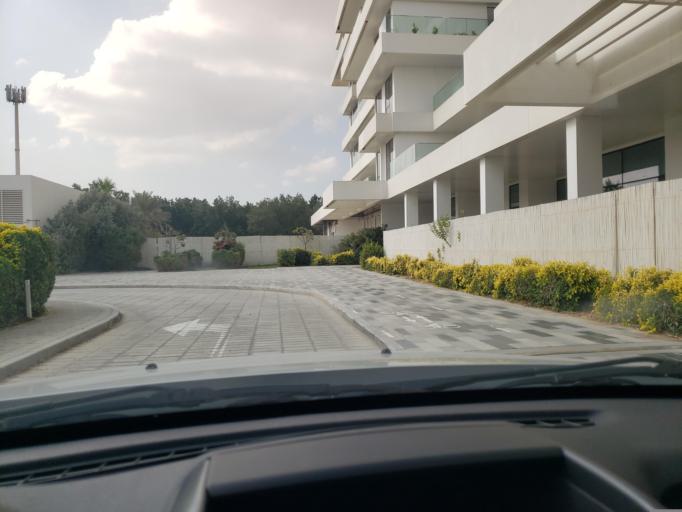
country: AE
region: Dubai
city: Dubai
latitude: 25.0991
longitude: 55.3149
